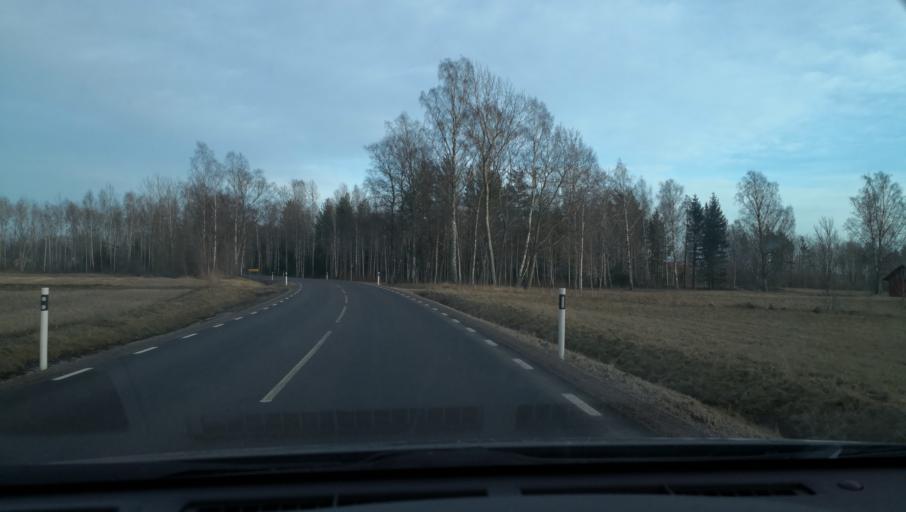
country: SE
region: Vaestra Goetaland
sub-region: Gullspangs Kommun
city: Gullspang
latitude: 59.0541
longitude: 14.2444
